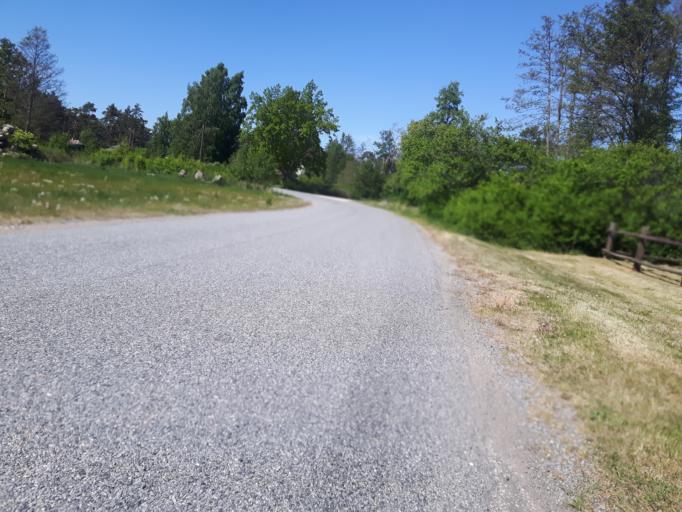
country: EE
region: Laeaene-Virumaa
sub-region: Haljala vald
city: Haljala
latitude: 59.5674
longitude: 26.2995
